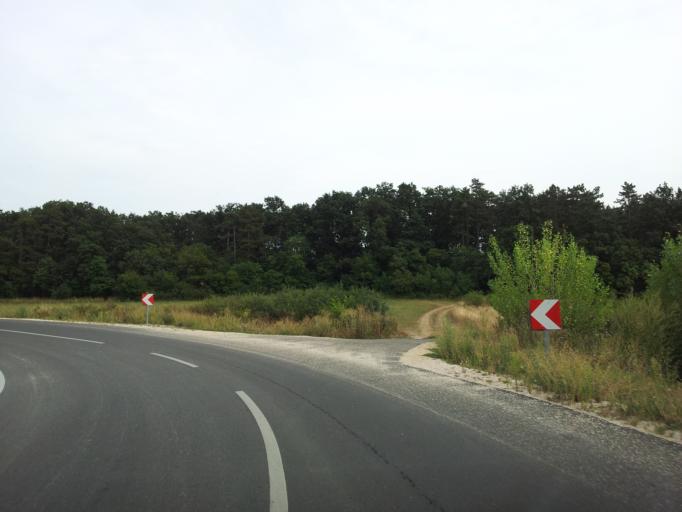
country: HU
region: Veszprem
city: Zanka
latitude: 46.9372
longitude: 17.7650
